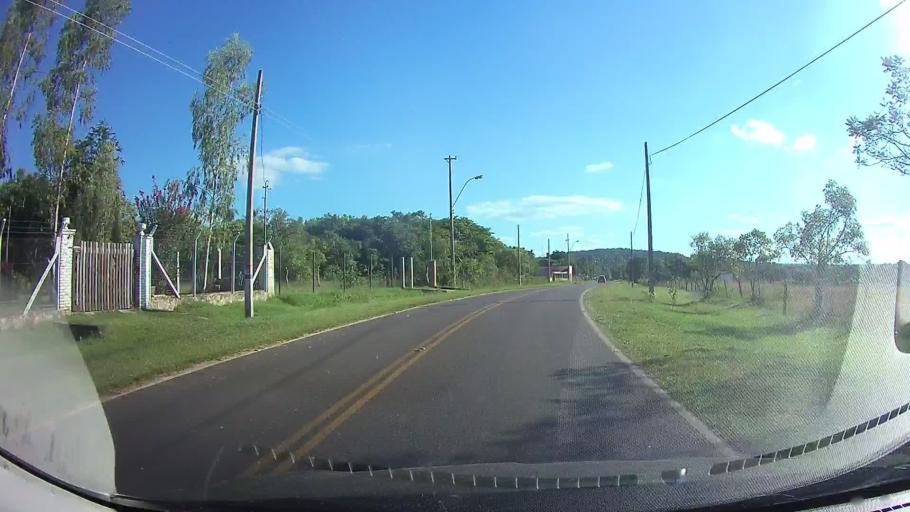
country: PY
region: Cordillera
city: Atyra
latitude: -25.3063
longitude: -57.1874
